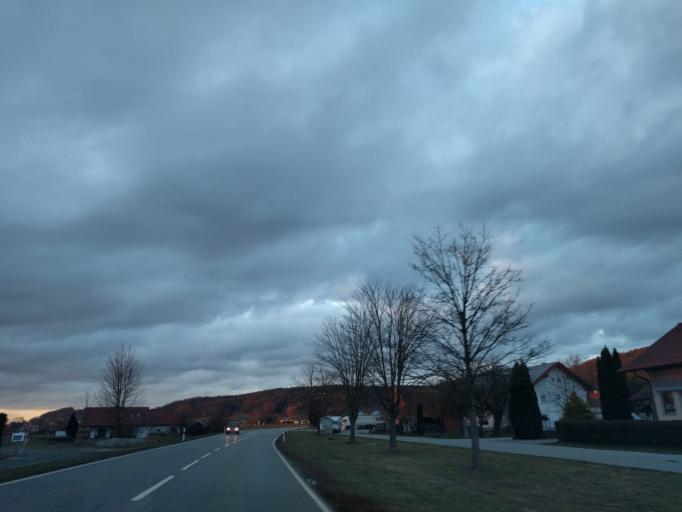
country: DE
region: Bavaria
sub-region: Lower Bavaria
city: Hofkirchen
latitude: 48.7063
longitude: 13.1081
